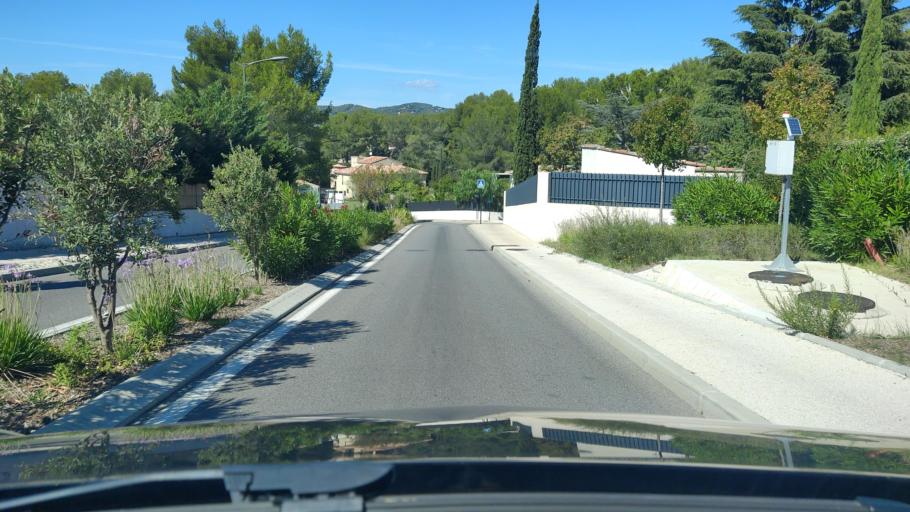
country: FR
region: Provence-Alpes-Cote d'Azur
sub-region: Departement du Var
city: Sanary-sur-Mer
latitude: 43.1385
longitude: 5.7845
